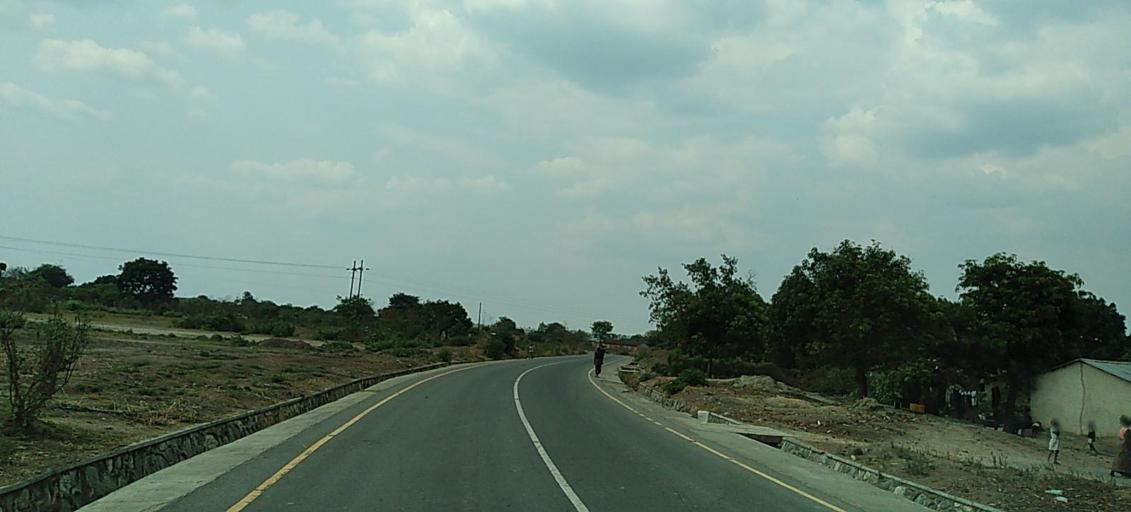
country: ZM
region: Copperbelt
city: Kalulushi
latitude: -12.8511
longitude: 28.1285
